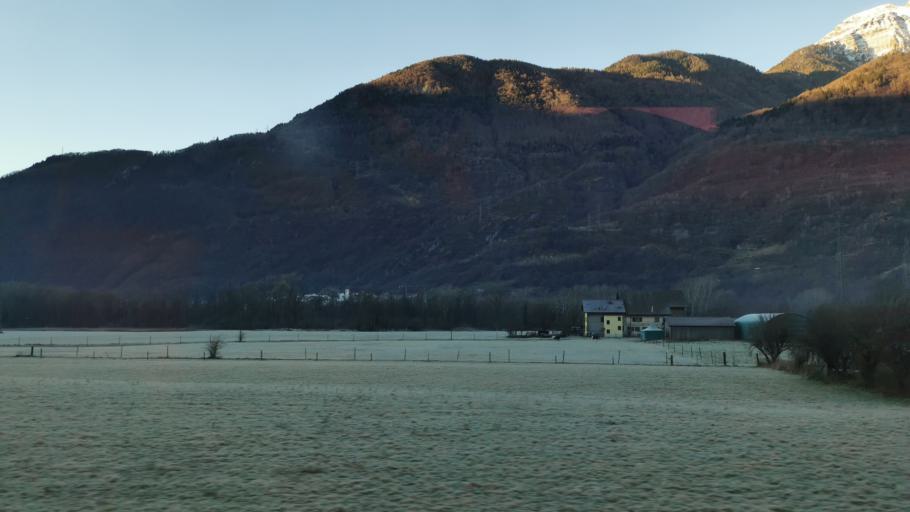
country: CH
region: Ticino
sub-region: Riviera District
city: Claro
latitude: 46.2428
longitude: 9.0297
